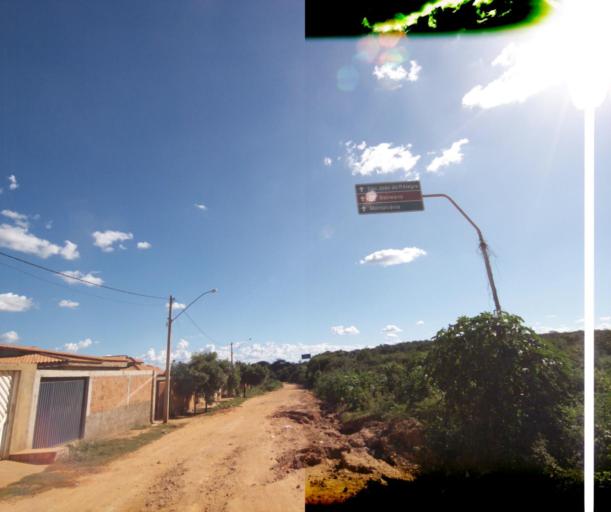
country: BR
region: Bahia
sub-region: Carinhanha
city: Carinhanha
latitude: -14.1850
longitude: -44.5426
